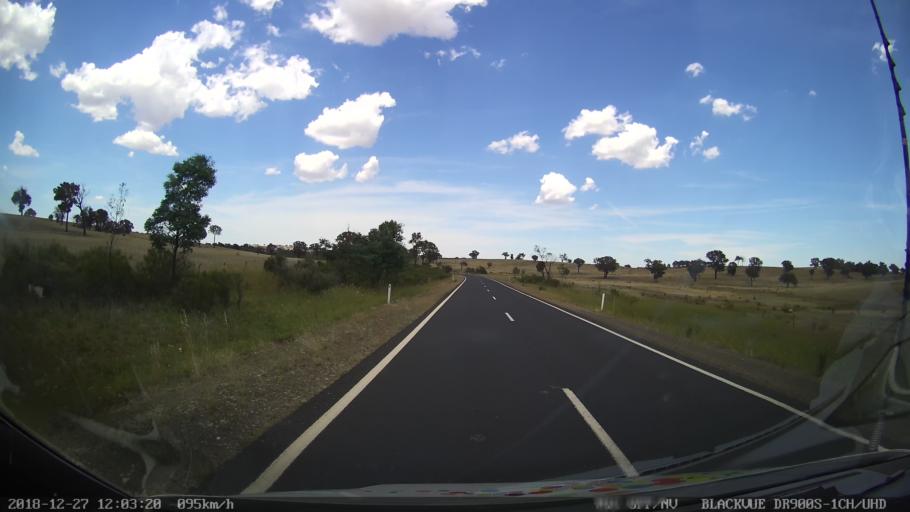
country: AU
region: New South Wales
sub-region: Blayney
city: Blayney
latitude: -33.7840
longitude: 149.3598
